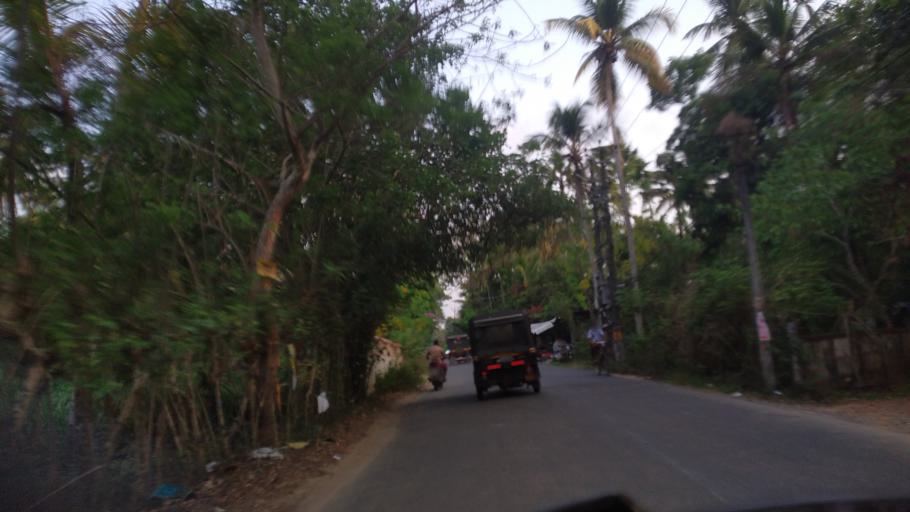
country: IN
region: Kerala
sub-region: Thrissur District
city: Kodungallur
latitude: 10.2463
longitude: 76.1491
